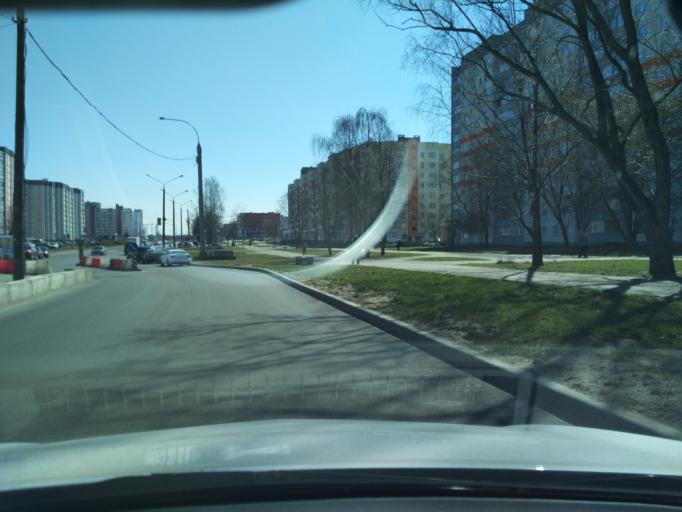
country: BY
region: Minsk
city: Minsk
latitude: 53.8821
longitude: 27.5504
